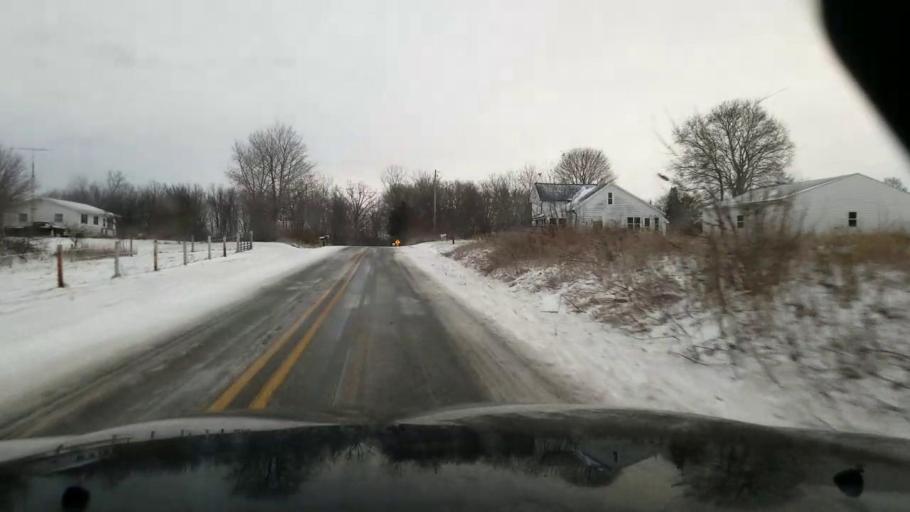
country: US
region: Michigan
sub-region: Jackson County
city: Vandercook Lake
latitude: 42.0904
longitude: -84.4658
